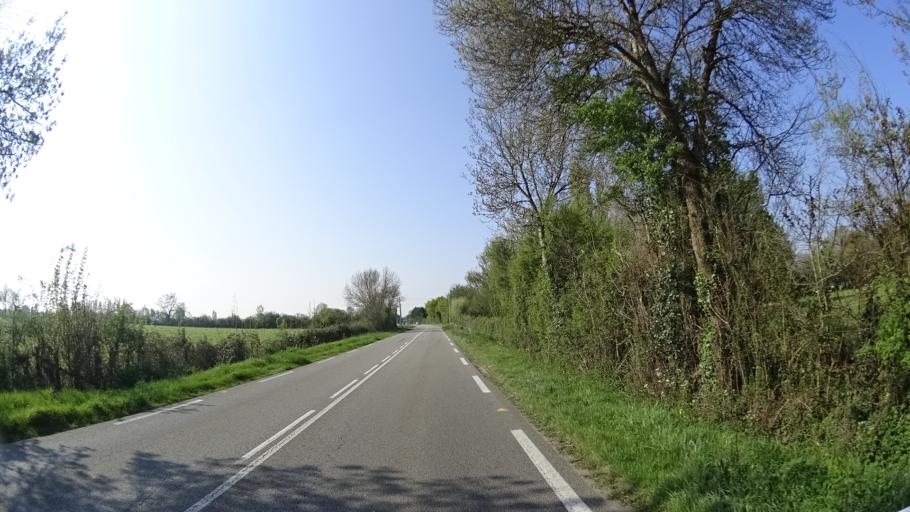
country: FR
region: Pays de la Loire
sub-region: Departement de la Loire-Atlantique
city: Port-Saint-Pere
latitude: 47.1249
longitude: -1.7632
